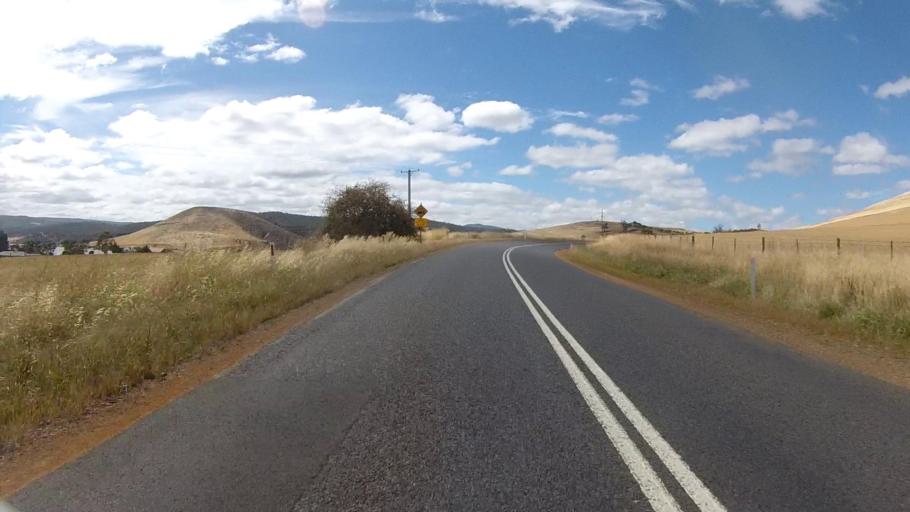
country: AU
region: Tasmania
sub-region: Brighton
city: Bridgewater
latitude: -42.5554
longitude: 147.3857
